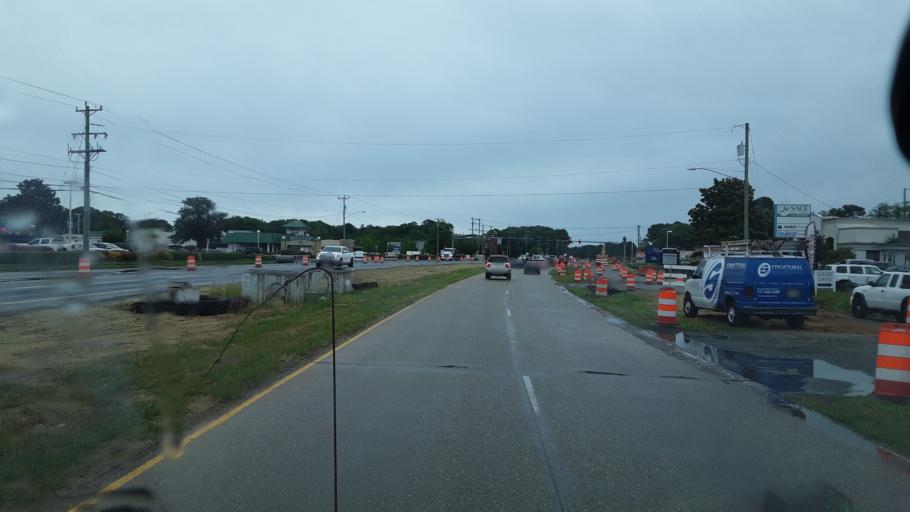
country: US
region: Virginia
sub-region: City of Virginia Beach
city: Virginia Beach
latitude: 36.8517
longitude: -76.0200
